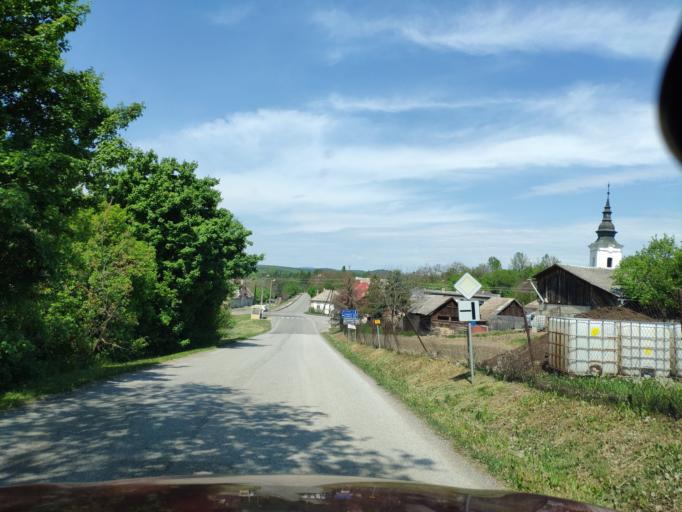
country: SK
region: Banskobystricky
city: Rimavska Sobota
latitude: 48.4692
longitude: 20.1019
